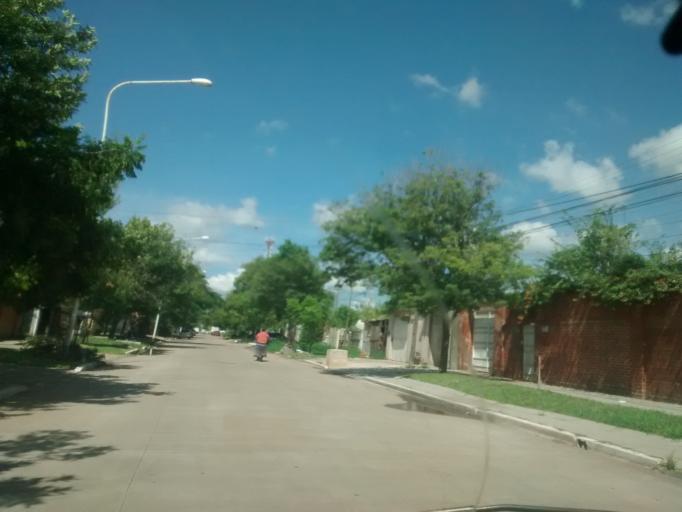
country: AR
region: Chaco
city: Resistencia
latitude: -27.4560
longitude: -59.0024
